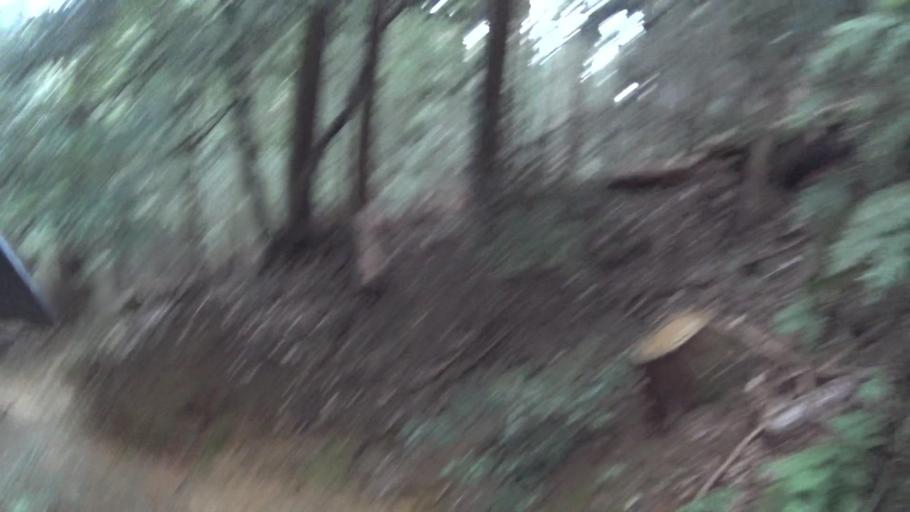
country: JP
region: Osaka
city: Kaizuka
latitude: 34.4696
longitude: 135.3022
